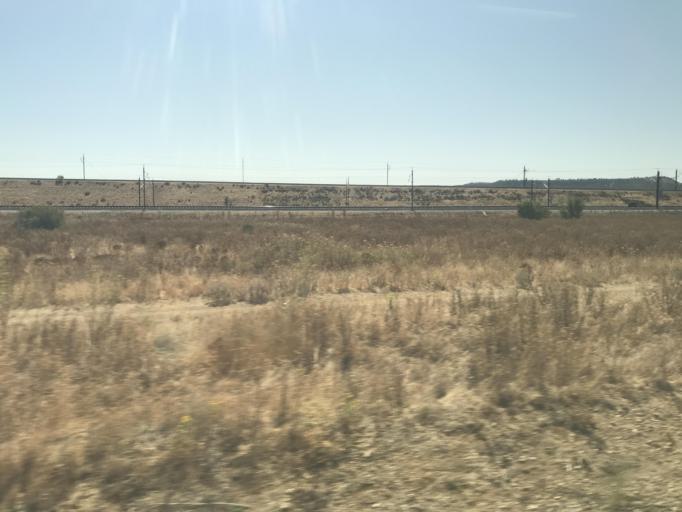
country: ES
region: Castille and Leon
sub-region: Provincia de Palencia
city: Venta de Banos
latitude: 41.9327
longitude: -4.4781
